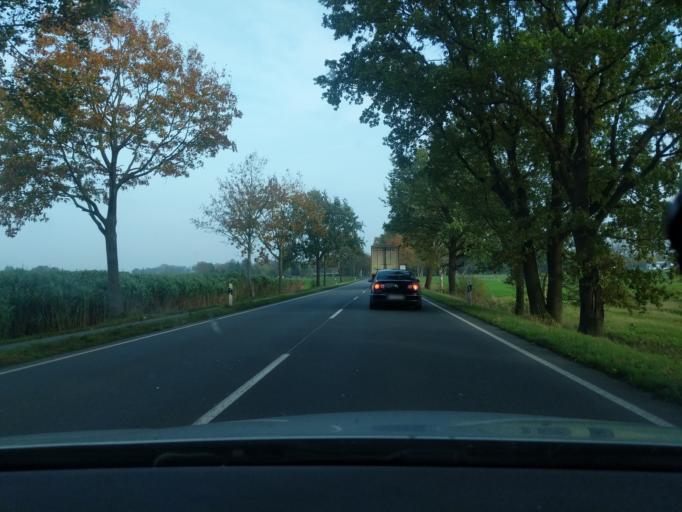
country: DE
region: Lower Saxony
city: Himmelpforten
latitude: 53.6128
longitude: 9.2889
